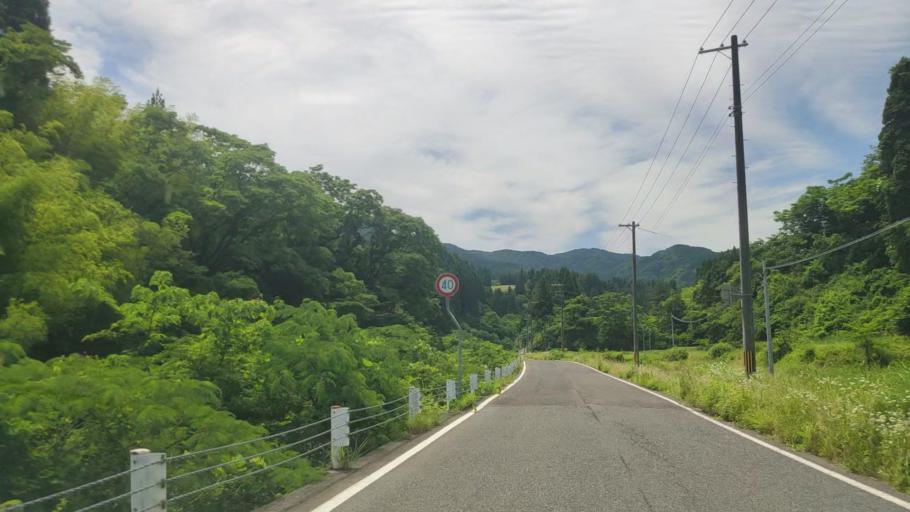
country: JP
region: Tottori
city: Tottori
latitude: 35.4280
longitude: 134.5284
